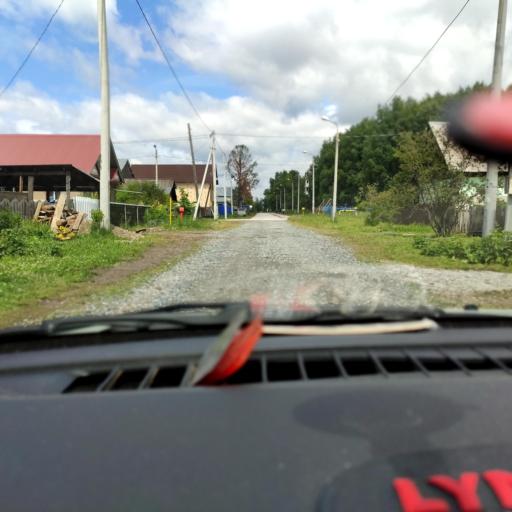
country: RU
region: Perm
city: Perm
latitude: 58.0763
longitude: 56.3581
